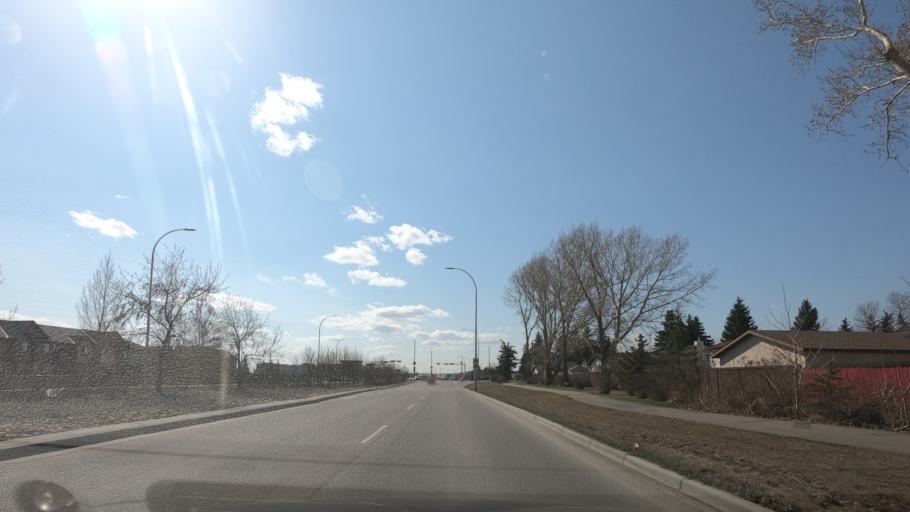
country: CA
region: Alberta
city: Airdrie
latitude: 51.2709
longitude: -113.9875
